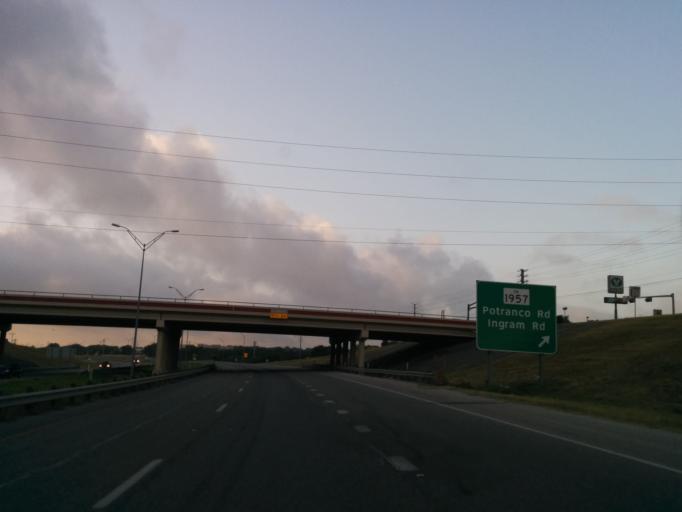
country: US
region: Texas
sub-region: Bexar County
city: Leon Valley
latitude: 29.4507
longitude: -98.6854
